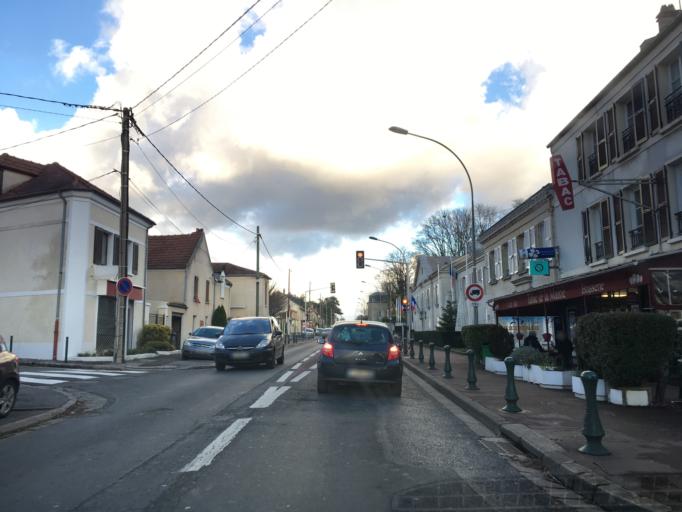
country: FR
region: Ile-de-France
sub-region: Departement du Val-de-Marne
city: Ormesson-sur-Marne
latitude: 48.7855
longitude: 2.5399
